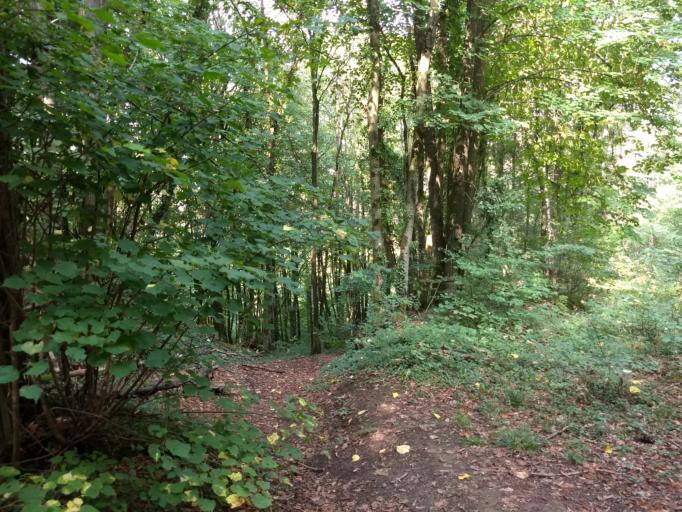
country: BE
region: Wallonia
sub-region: Province de Namur
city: Beauraing
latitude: 50.1128
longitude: 5.0183
